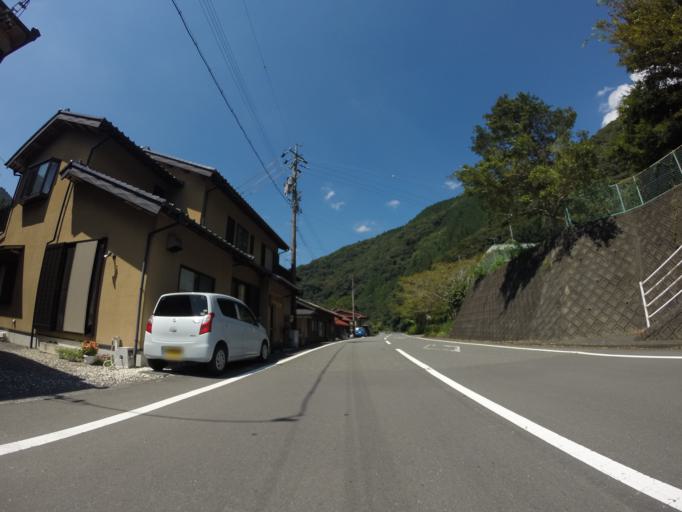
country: JP
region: Shizuoka
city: Shizuoka-shi
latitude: 35.0484
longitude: 138.2468
